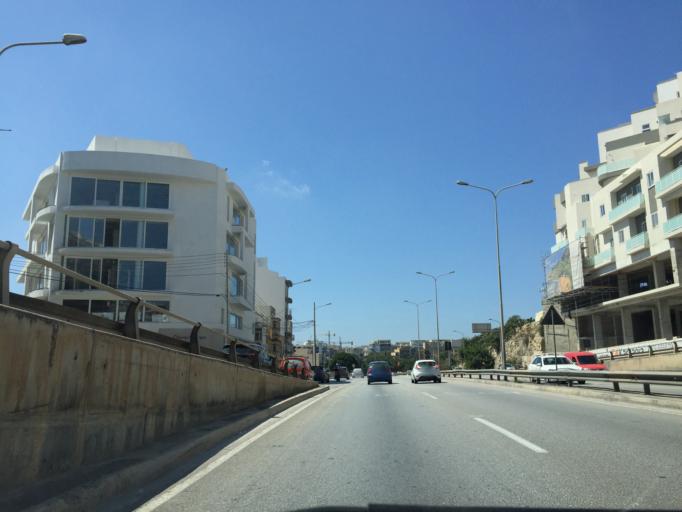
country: MT
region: L-Imsida
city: Imsida
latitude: 35.8982
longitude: 14.4841
